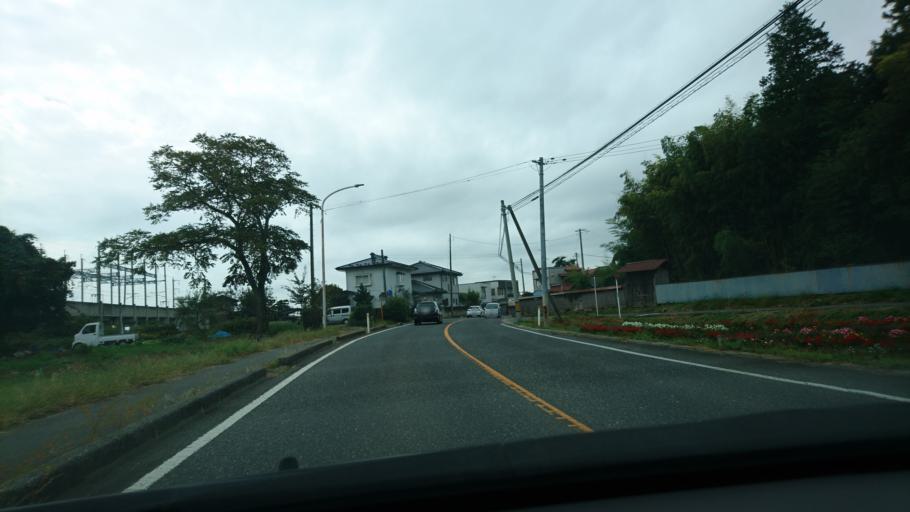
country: JP
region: Iwate
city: Ichinoseki
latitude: 38.7604
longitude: 141.0775
